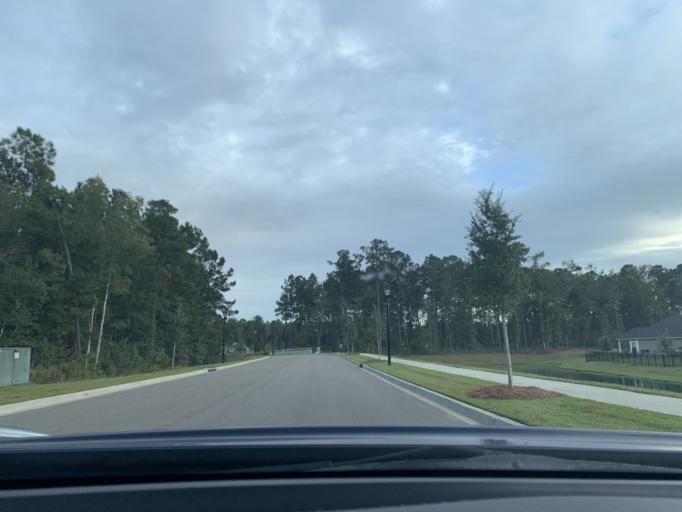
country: US
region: Georgia
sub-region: Chatham County
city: Pooler
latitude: 32.0713
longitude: -81.2583
